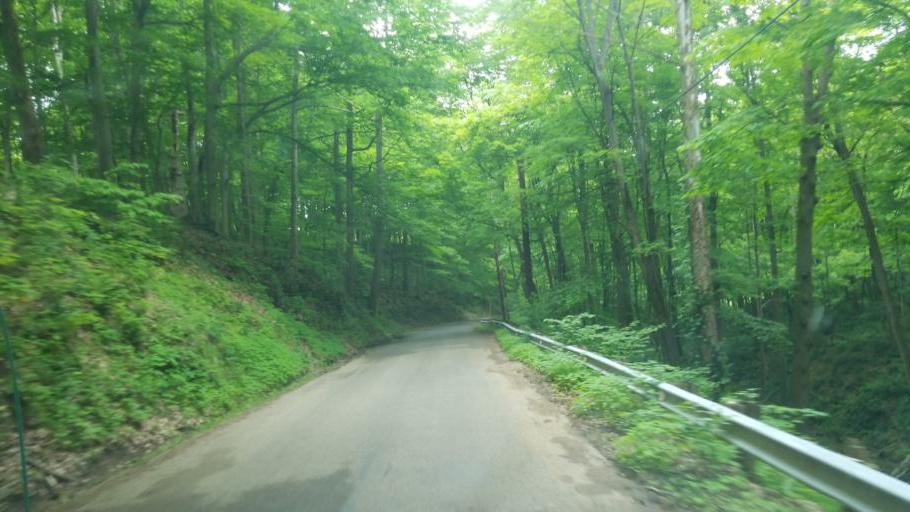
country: US
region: Ohio
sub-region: Sandusky County
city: Bellville
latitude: 40.6470
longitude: -82.4006
